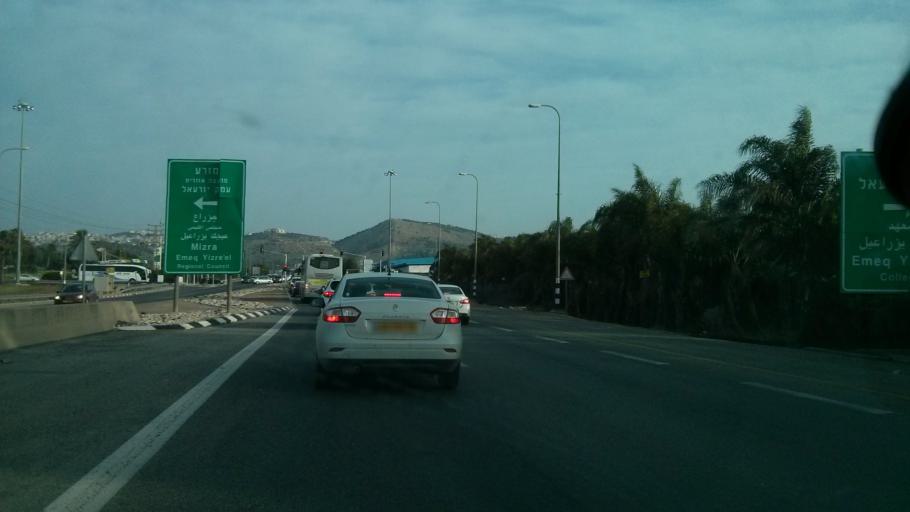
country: IL
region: Northern District
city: `Afula `Illit
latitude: 32.6472
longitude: 35.2916
